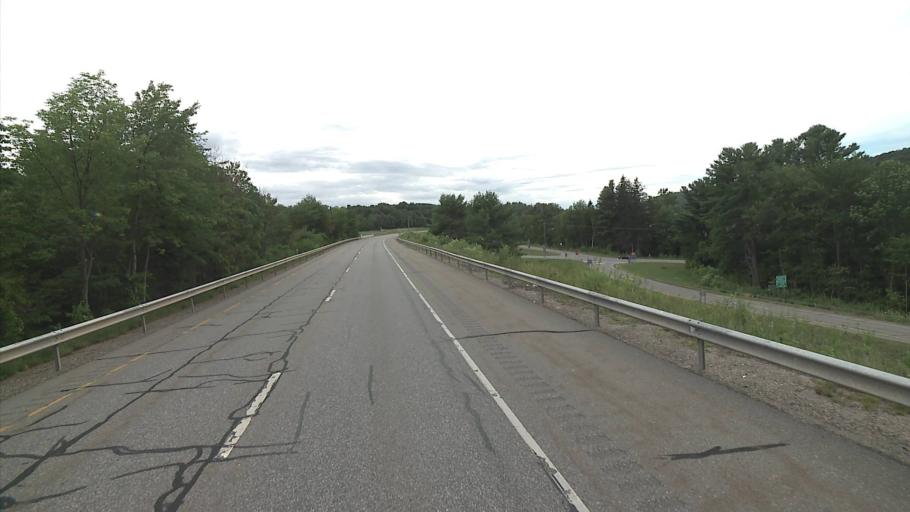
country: US
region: Connecticut
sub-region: Litchfield County
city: Winsted
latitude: 41.8799
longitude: -73.0718
